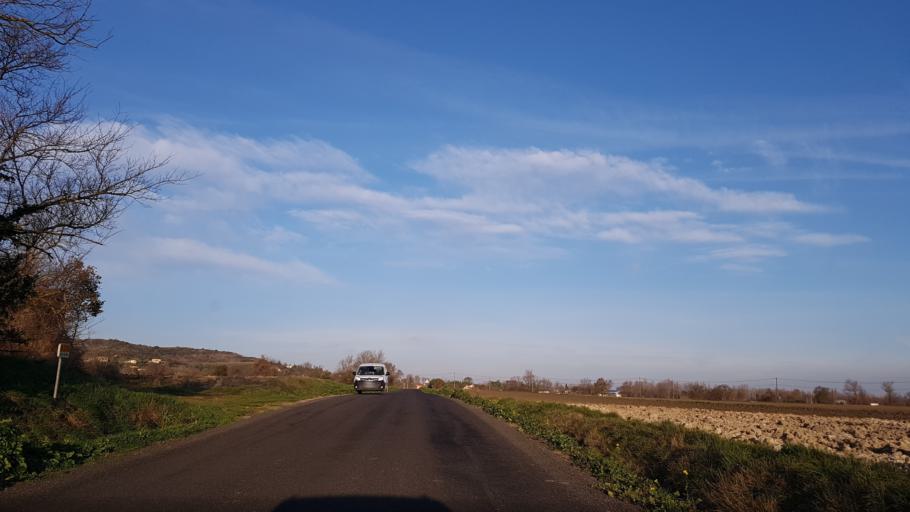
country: FR
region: Languedoc-Roussillon
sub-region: Departement de l'Aude
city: Villeneuve-la-Comptal
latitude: 43.2871
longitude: 1.9314
